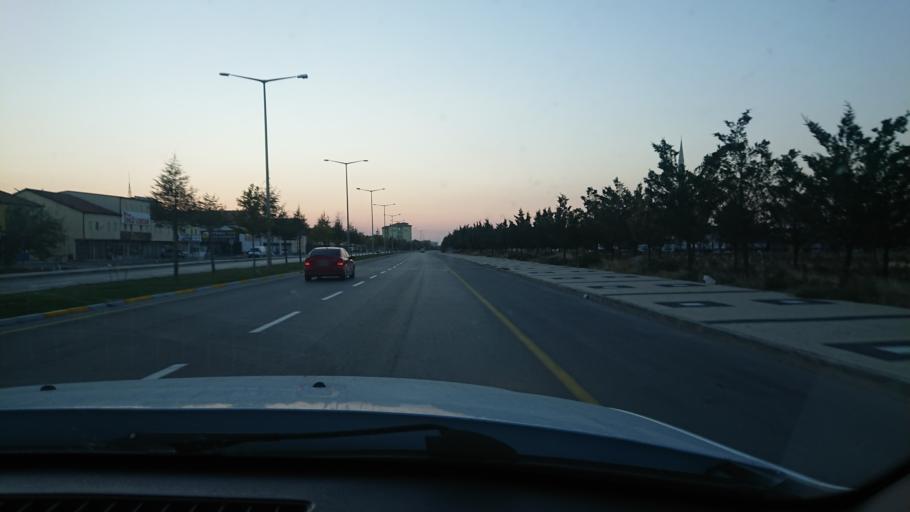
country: TR
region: Aksaray
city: Aksaray
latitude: 38.3572
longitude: 33.9877
